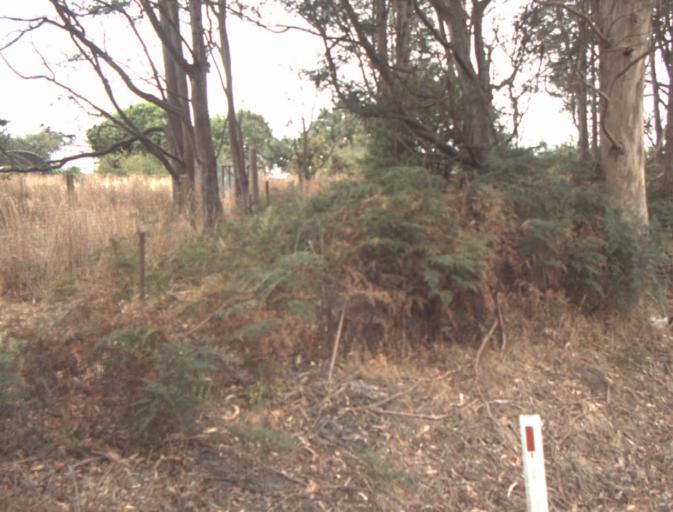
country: AU
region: Tasmania
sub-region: Launceston
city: Mayfield
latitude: -41.1702
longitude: 147.2130
